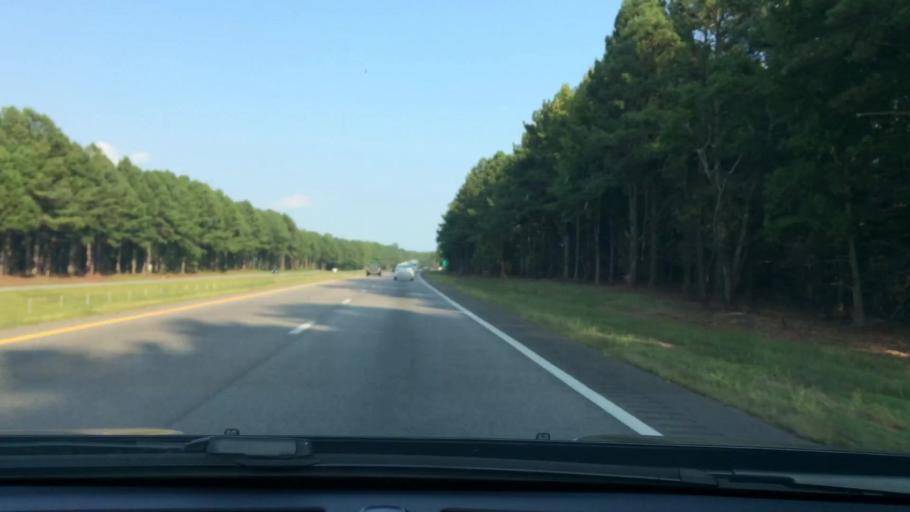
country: US
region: North Carolina
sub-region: Wake County
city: Zebulon
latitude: 35.8074
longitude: -78.2143
